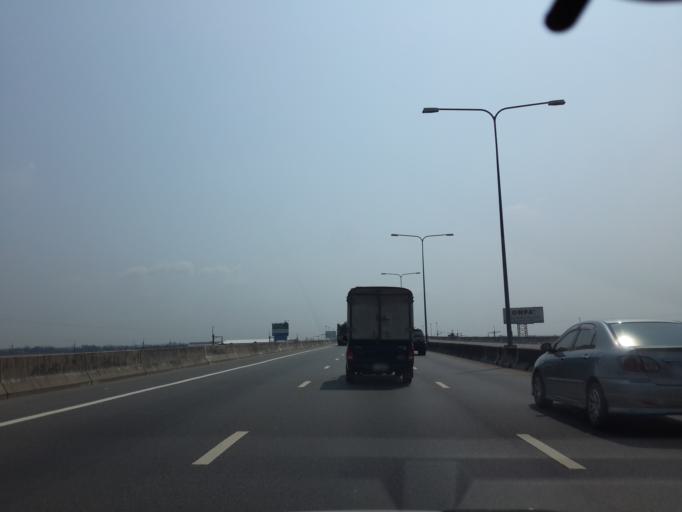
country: TH
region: Samut Prakan
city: Bang Bo
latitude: 13.5830
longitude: 100.8607
